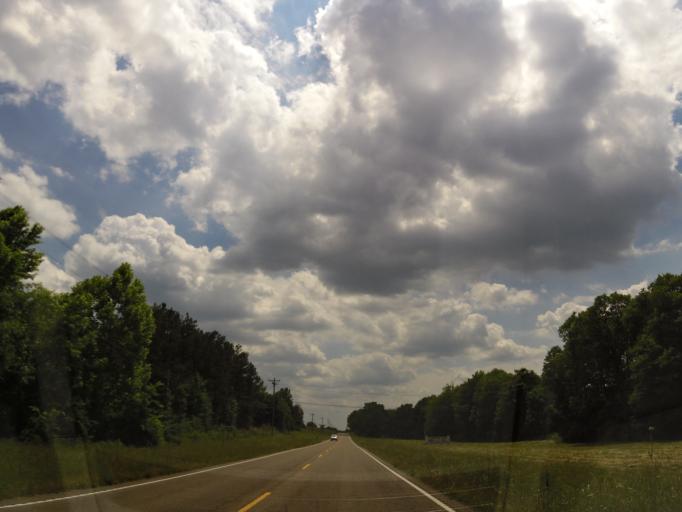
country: US
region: Tennessee
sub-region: Bledsoe County
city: Pikeville
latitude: 35.5349
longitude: -85.2641
